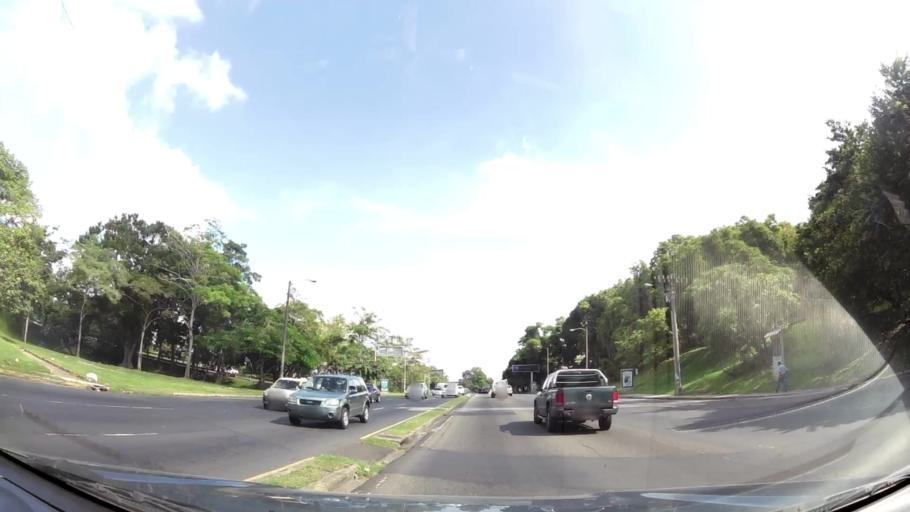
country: PA
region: Panama
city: Panama
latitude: 8.9788
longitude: -79.5372
